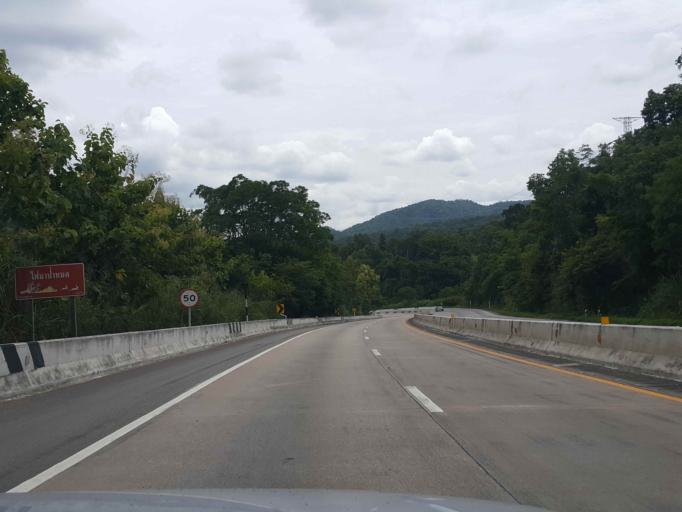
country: TH
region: Lamphun
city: Mae Tha
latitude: 18.4192
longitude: 99.2095
